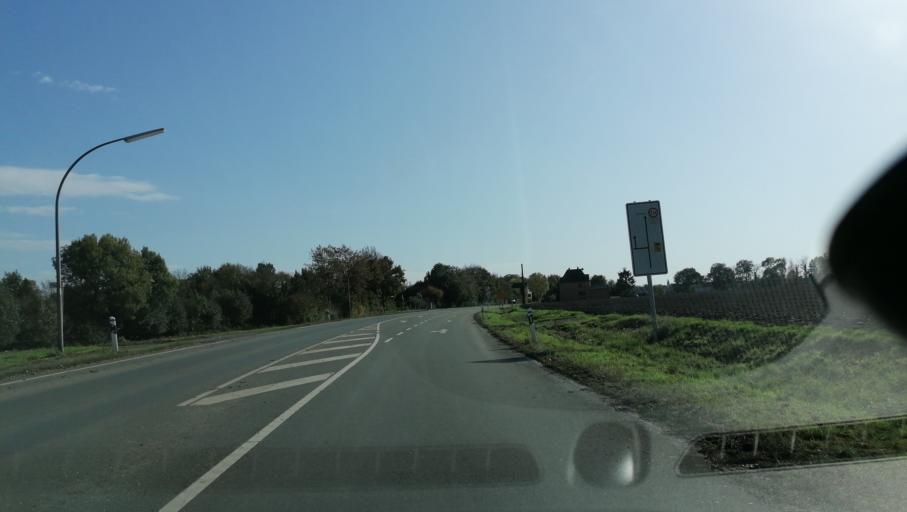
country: DE
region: North Rhine-Westphalia
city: Waltrop
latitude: 51.6173
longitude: 7.4343
